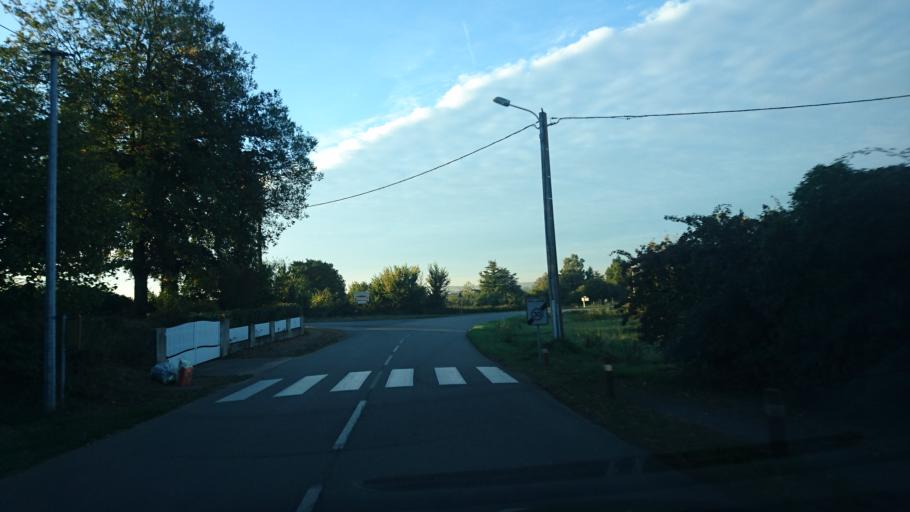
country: FR
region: Brittany
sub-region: Departement d'Ille-et-Vilaine
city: Sainte-Marie
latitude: 47.7184
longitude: -1.9777
